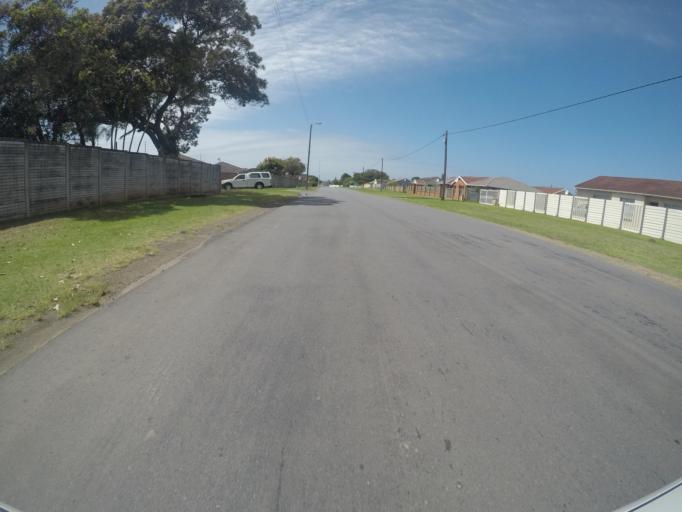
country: ZA
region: Eastern Cape
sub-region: Buffalo City Metropolitan Municipality
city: East London
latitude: -32.9510
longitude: 27.9975
